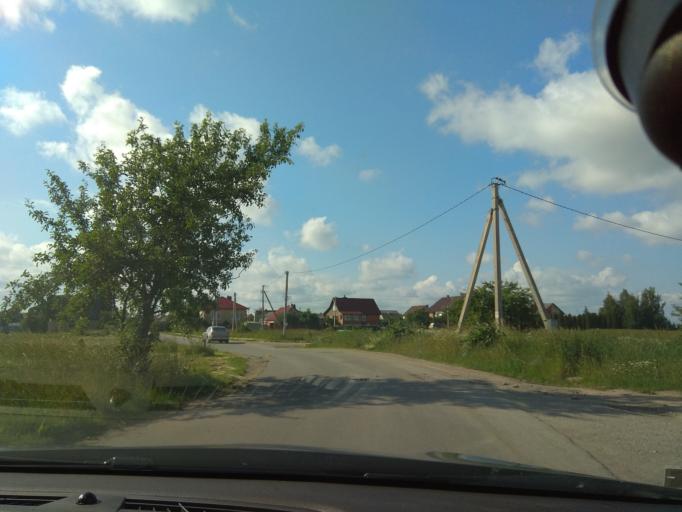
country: LT
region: Siauliu apskritis
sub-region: Joniskis
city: Joniskis
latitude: 56.2439
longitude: 23.6279
